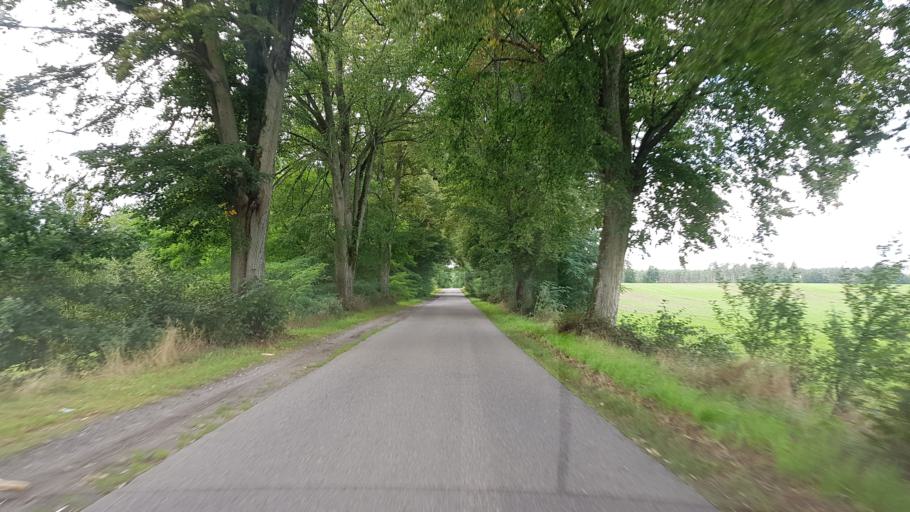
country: PL
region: West Pomeranian Voivodeship
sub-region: Powiat bialogardzki
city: Tychowo
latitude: 54.0254
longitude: 16.3573
